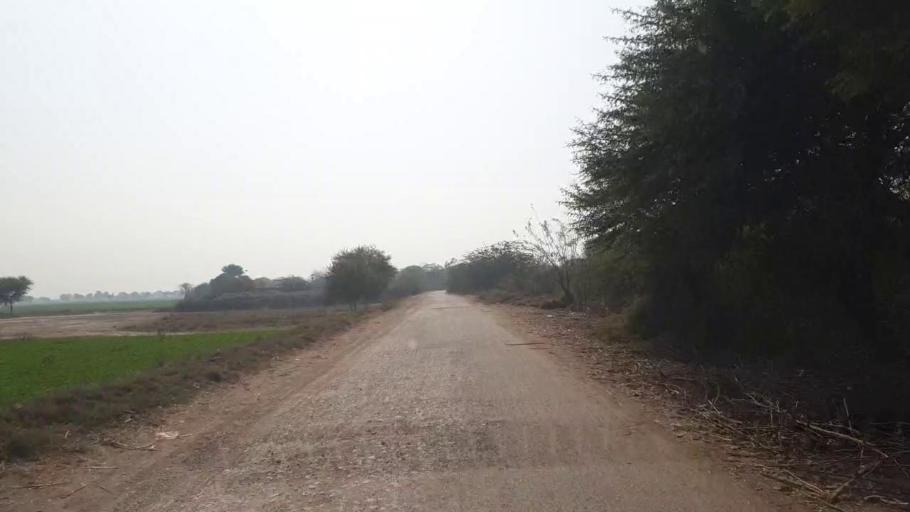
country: PK
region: Sindh
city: Hala
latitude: 25.8949
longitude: 68.4414
